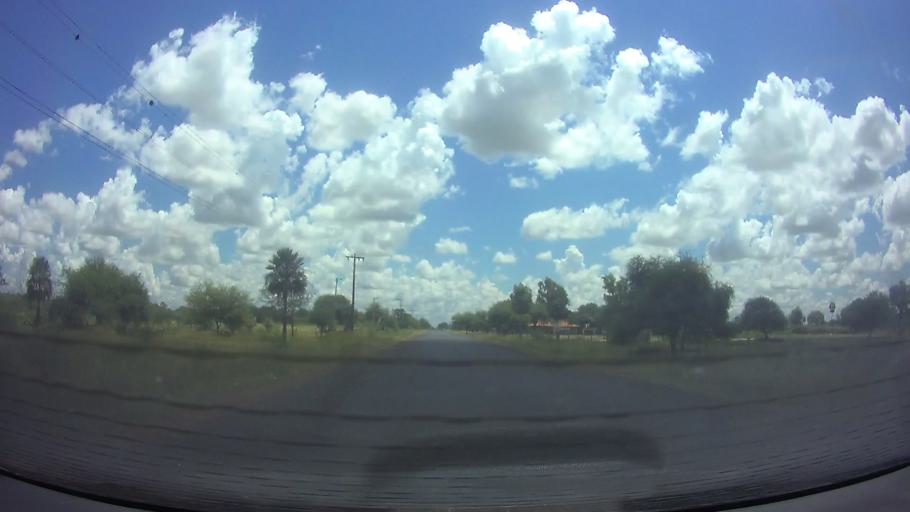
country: PY
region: Presidente Hayes
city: Nanawa
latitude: -25.2409
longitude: -57.6819
